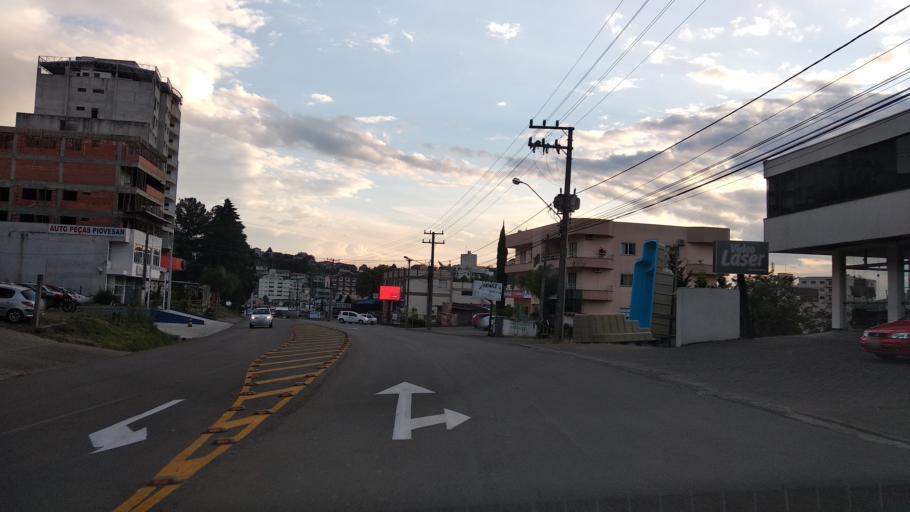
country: BR
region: Santa Catarina
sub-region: Videira
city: Videira
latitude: -27.0033
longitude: -51.1356
